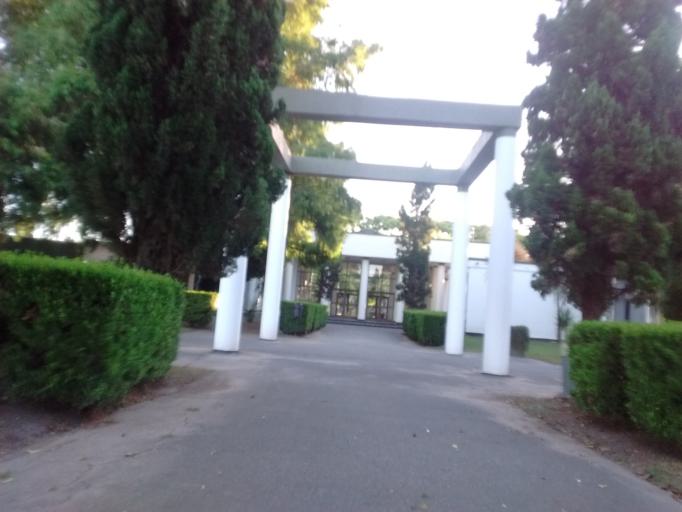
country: AR
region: Santa Fe
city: Funes
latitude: -32.9193
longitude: -60.7914
